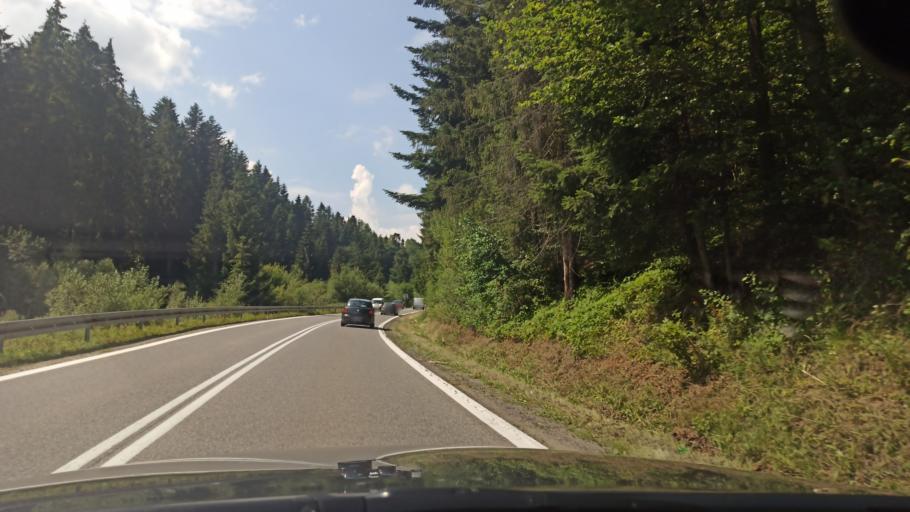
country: PL
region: Lesser Poland Voivodeship
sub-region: Powiat nowotarski
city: Krosnica
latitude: 49.4419
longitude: 20.3535
